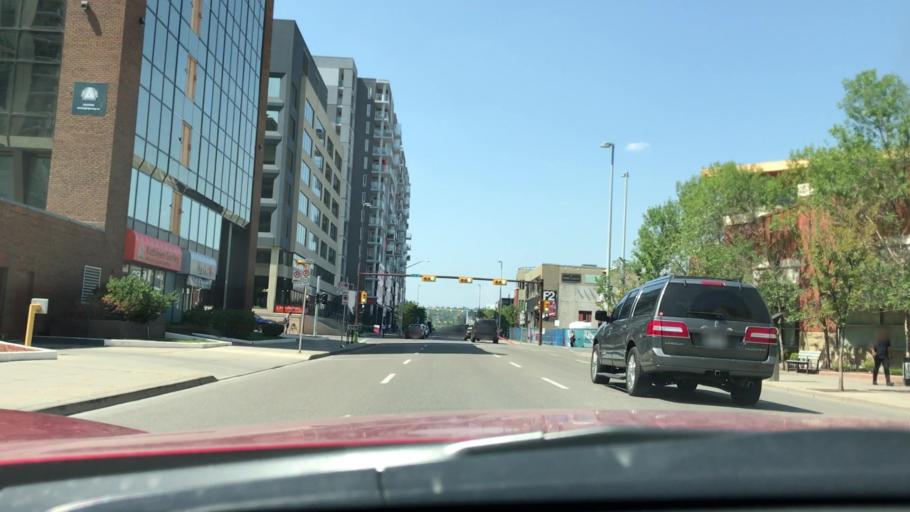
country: CA
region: Alberta
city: Calgary
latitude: 51.0431
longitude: -114.0880
